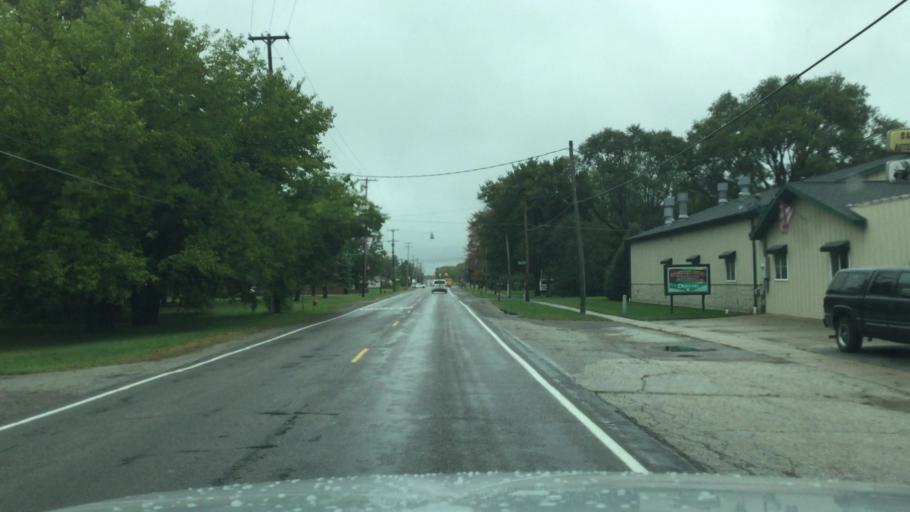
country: US
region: Michigan
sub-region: Saginaw County
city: Carrollton
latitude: 43.4762
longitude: -83.9458
